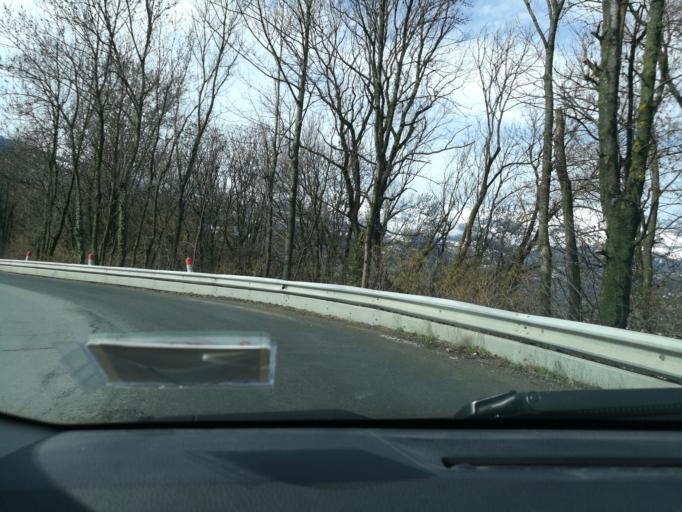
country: FR
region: Rhone-Alpes
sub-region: Departement de la Haute-Savoie
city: Saint-Gervais-les-Bains
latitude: 45.9106
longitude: 6.7188
